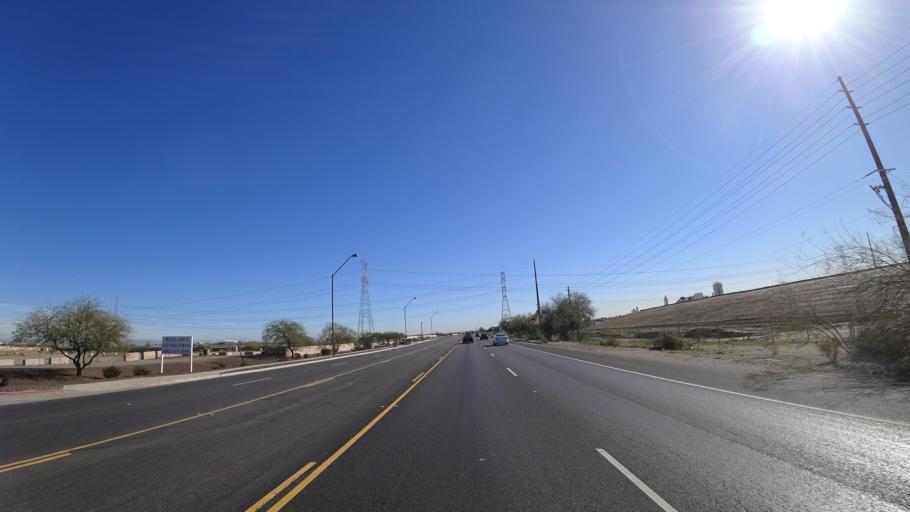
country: US
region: Arizona
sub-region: Maricopa County
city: Litchfield Park
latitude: 33.4932
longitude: -112.3216
